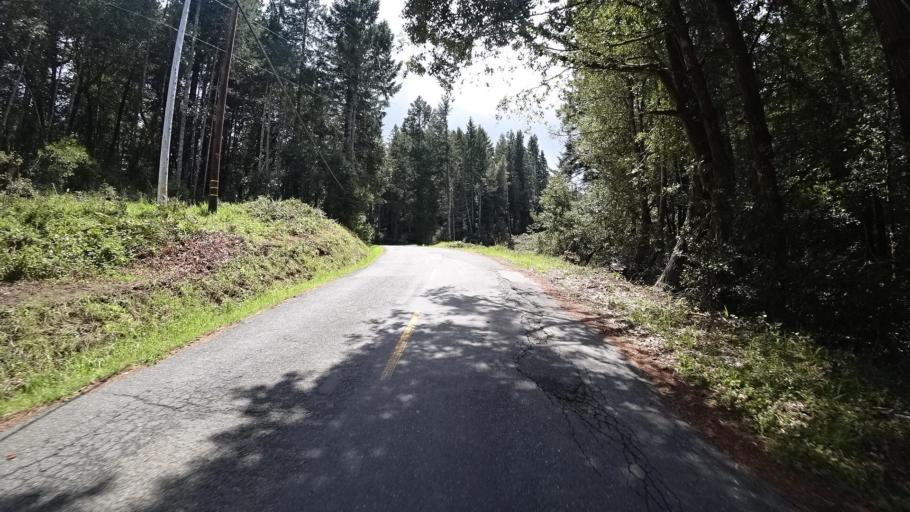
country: US
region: California
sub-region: Humboldt County
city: Blue Lake
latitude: 40.7609
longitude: -123.9629
